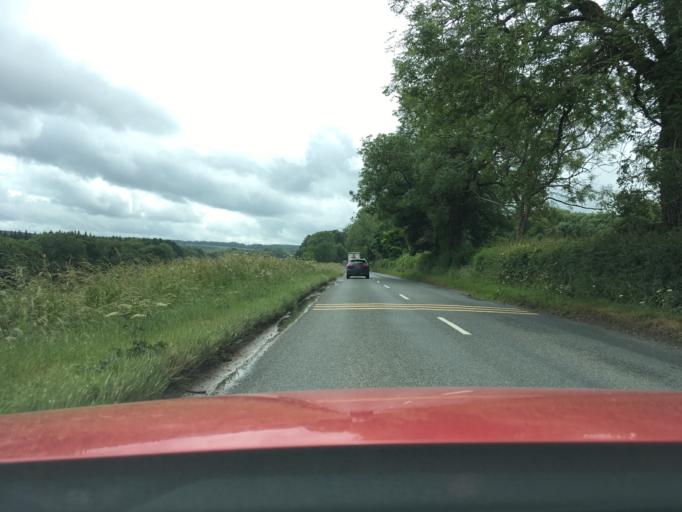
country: GB
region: England
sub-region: Gloucestershire
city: Chipping Campden
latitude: 52.0508
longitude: -1.8022
